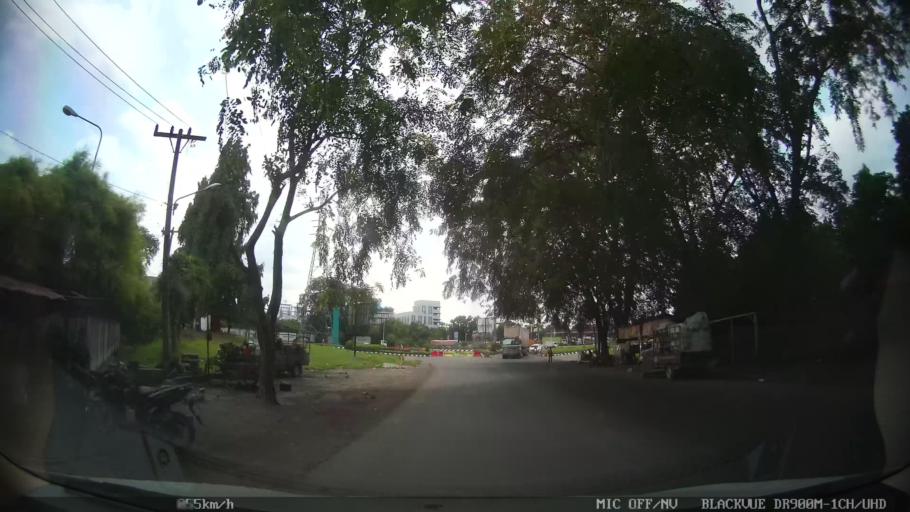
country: ID
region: North Sumatra
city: Labuhan Deli
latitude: 3.6745
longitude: 98.6837
